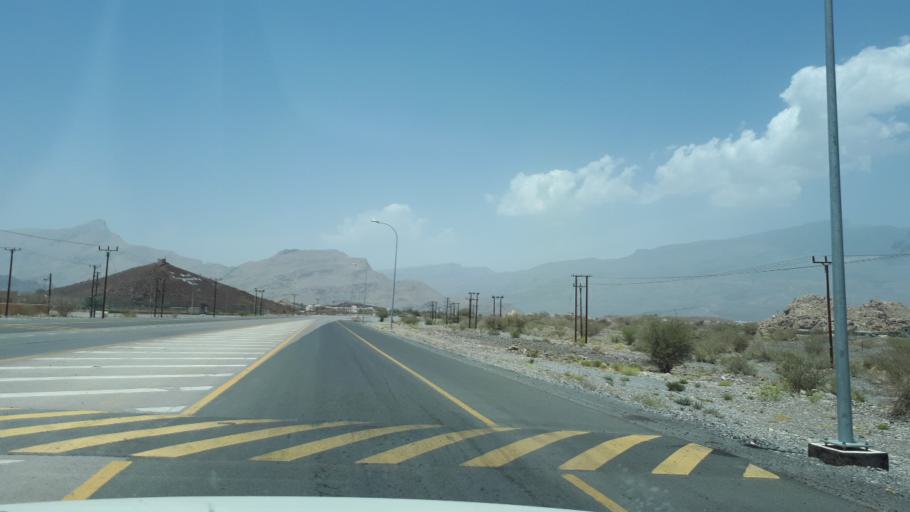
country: OM
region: Muhafazat ad Dakhiliyah
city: Bahla'
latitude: 23.0653
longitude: 57.2771
